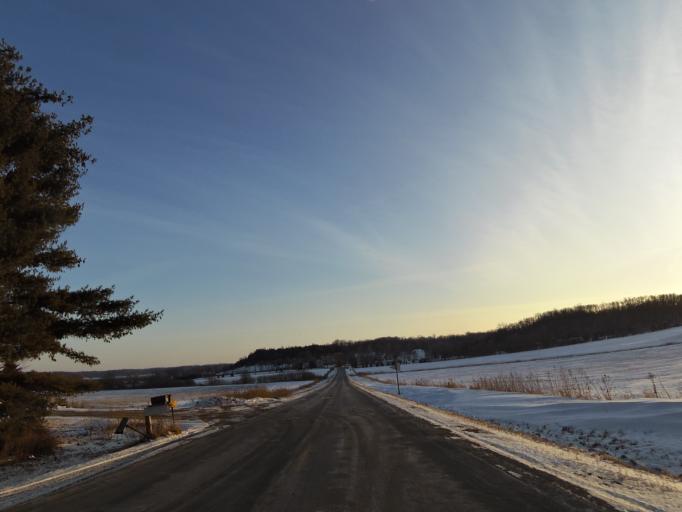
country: US
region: Wisconsin
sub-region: Pierce County
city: River Falls
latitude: 44.9036
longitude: -92.6089
